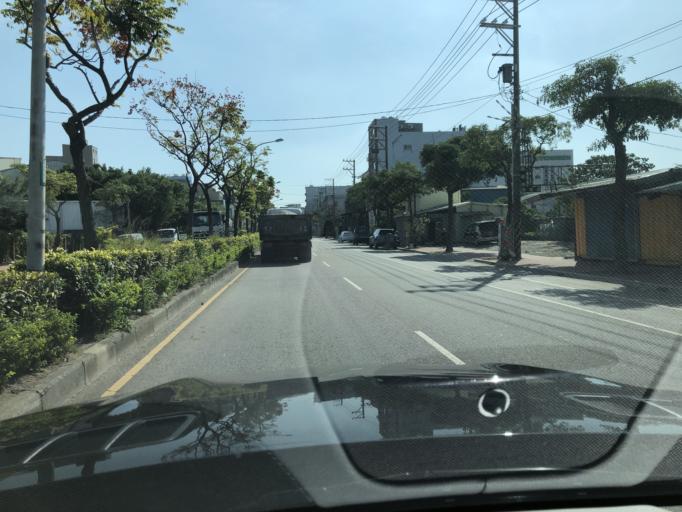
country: TW
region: Taiwan
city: Taoyuan City
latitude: 25.0750
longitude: 121.2852
